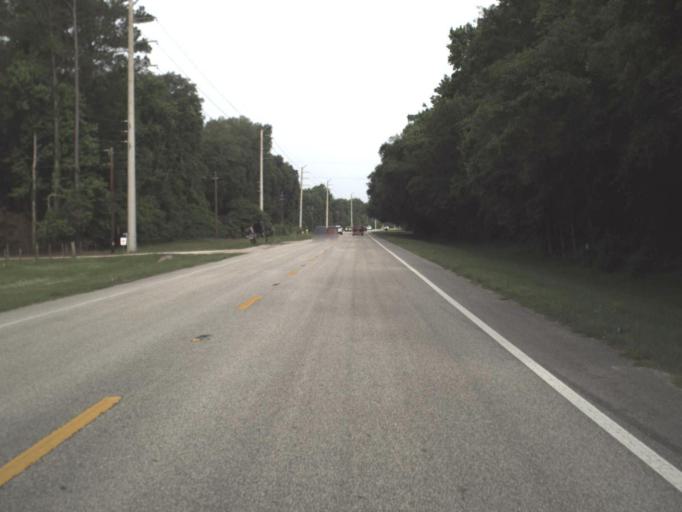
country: US
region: Florida
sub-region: Saint Johns County
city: Saint Augustine
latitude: 29.9472
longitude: -81.4469
